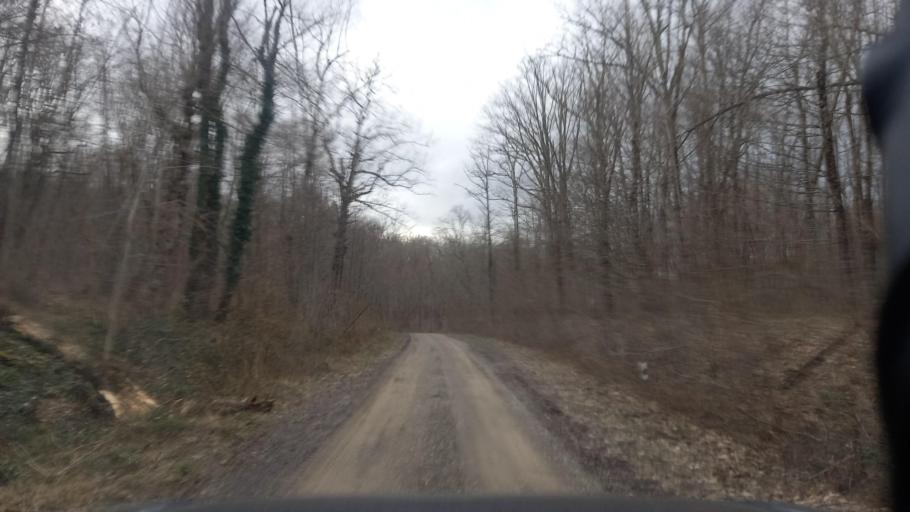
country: RU
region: Krasnodarskiy
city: Dzhubga
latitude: 44.4855
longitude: 38.7758
